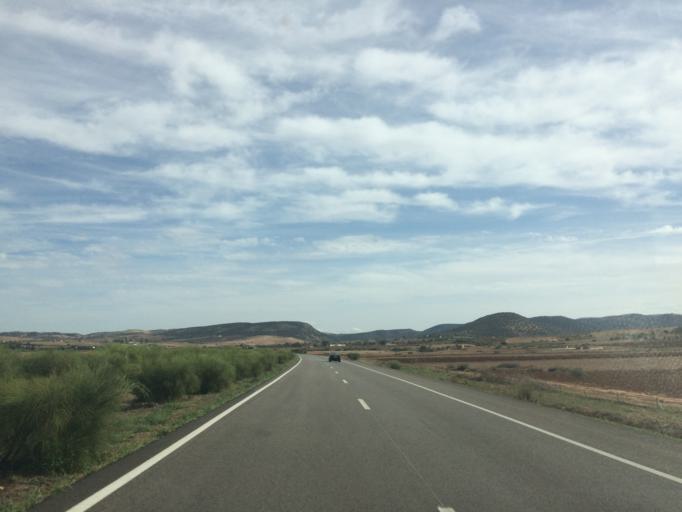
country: MA
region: Rabat-Sale-Zemmour-Zaer
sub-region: Khemisset
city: Khemisset
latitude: 33.7840
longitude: -5.9083
